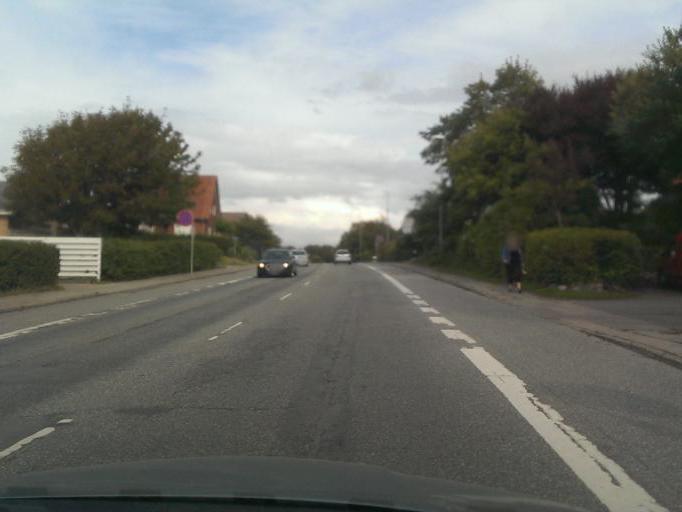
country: DK
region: North Denmark
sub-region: Hjorring Kommune
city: Hjorring
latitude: 57.4664
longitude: 9.9764
